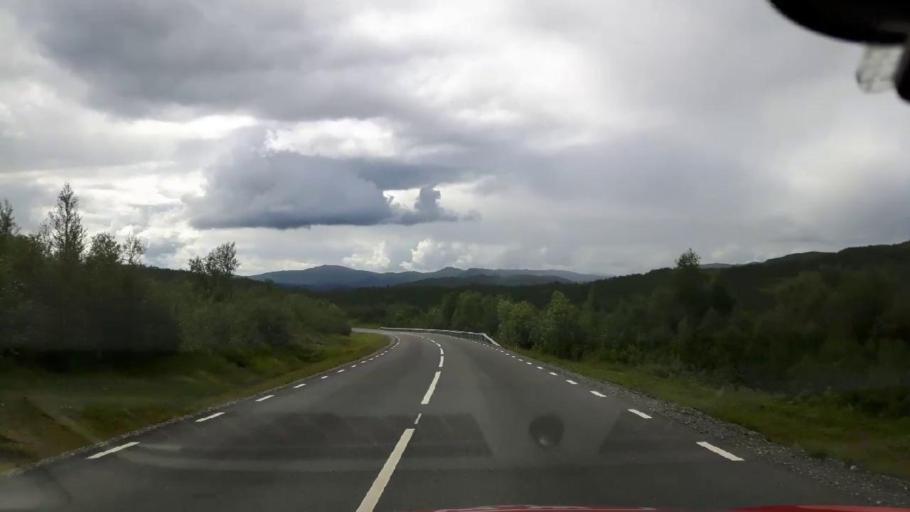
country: NO
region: Nordland
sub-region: Hattfjelldal
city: Hattfjelldal
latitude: 64.9863
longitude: 14.2138
